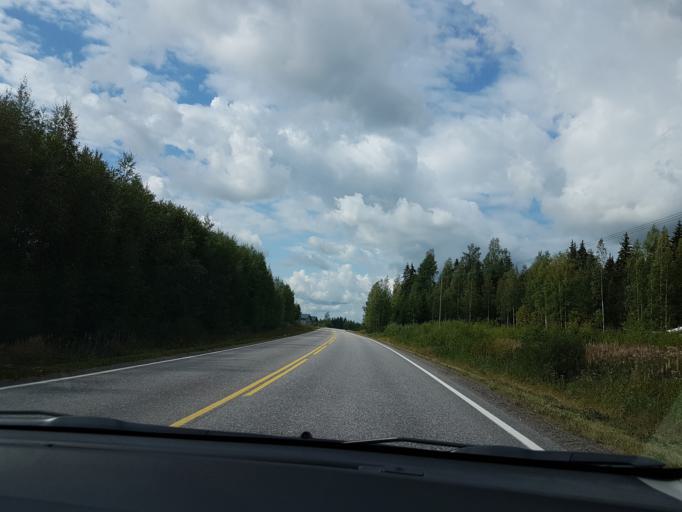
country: FI
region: Uusimaa
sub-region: Helsinki
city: Pornainen
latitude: 60.4763
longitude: 25.3187
